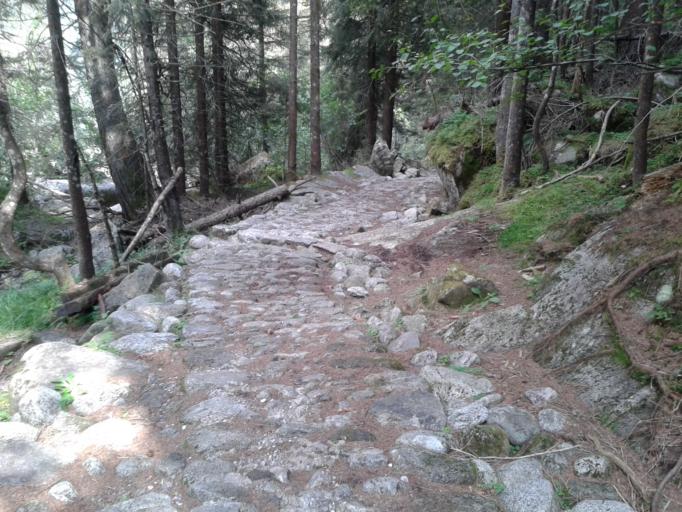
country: IT
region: Trentino-Alto Adige
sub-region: Provincia di Trento
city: Daone
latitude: 46.0031
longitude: 10.5078
